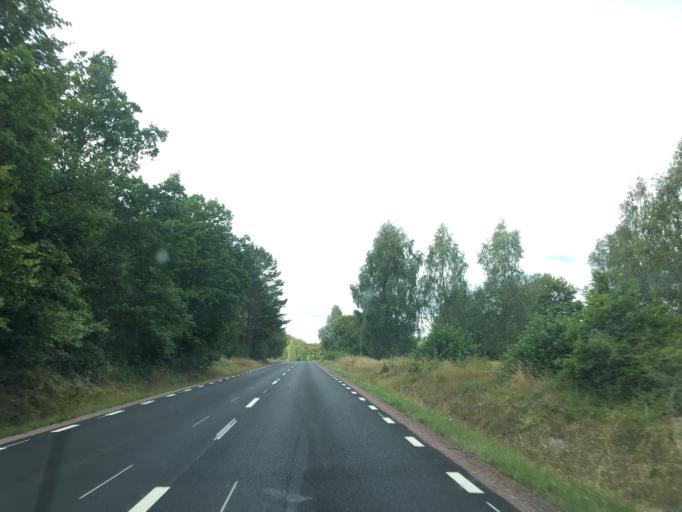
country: SE
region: Kalmar
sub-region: Nybro Kommun
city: Nybro
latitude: 56.9183
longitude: 15.9781
